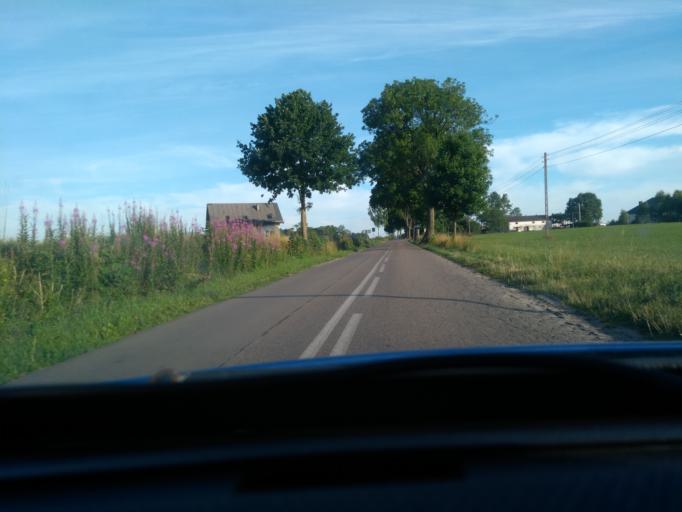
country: PL
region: Pomeranian Voivodeship
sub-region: Powiat kartuski
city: Przodkowo
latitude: 54.3961
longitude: 18.3386
